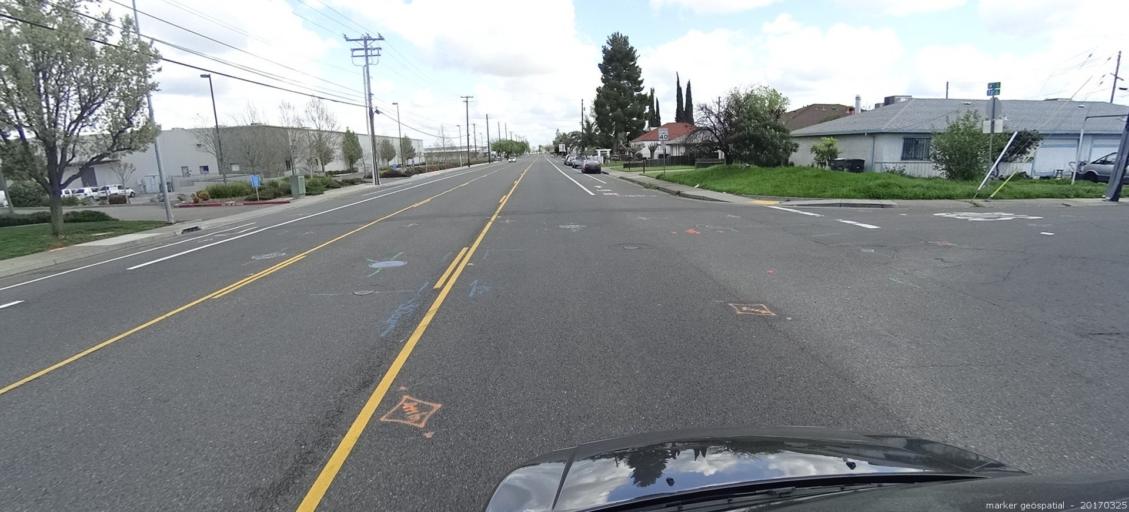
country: US
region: California
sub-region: Sacramento County
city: Florin
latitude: 38.5396
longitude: -121.4193
